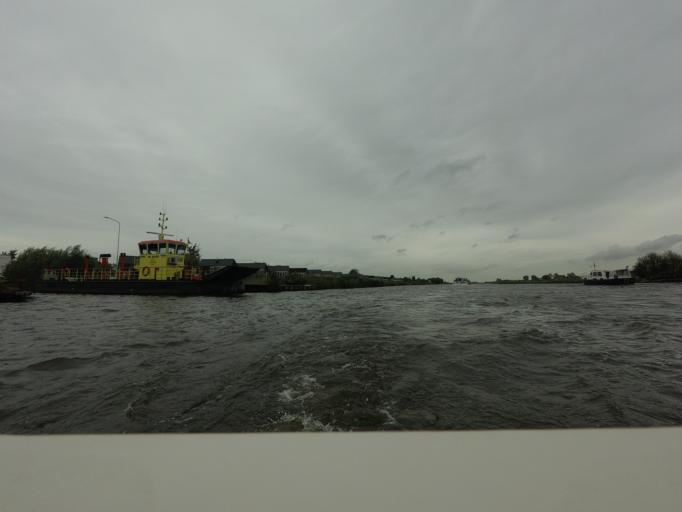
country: NL
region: Friesland
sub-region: Gemeente Boarnsterhim
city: Grou
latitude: 53.1005
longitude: 5.8497
